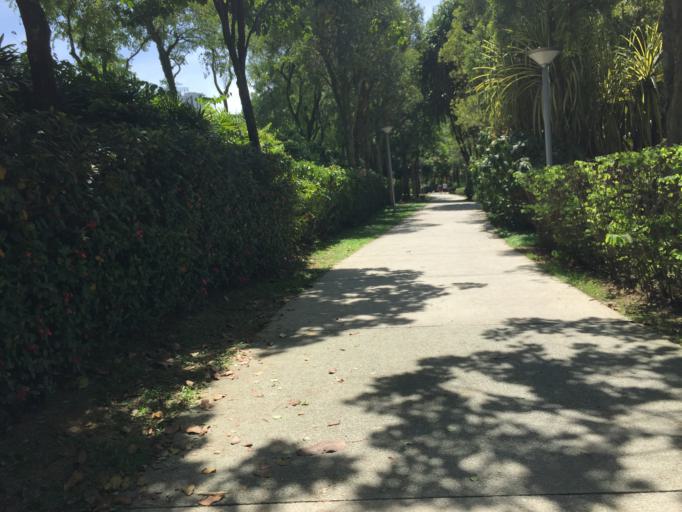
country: MY
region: Kuala Lumpur
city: Kuala Lumpur
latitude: 3.1867
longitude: 101.6307
